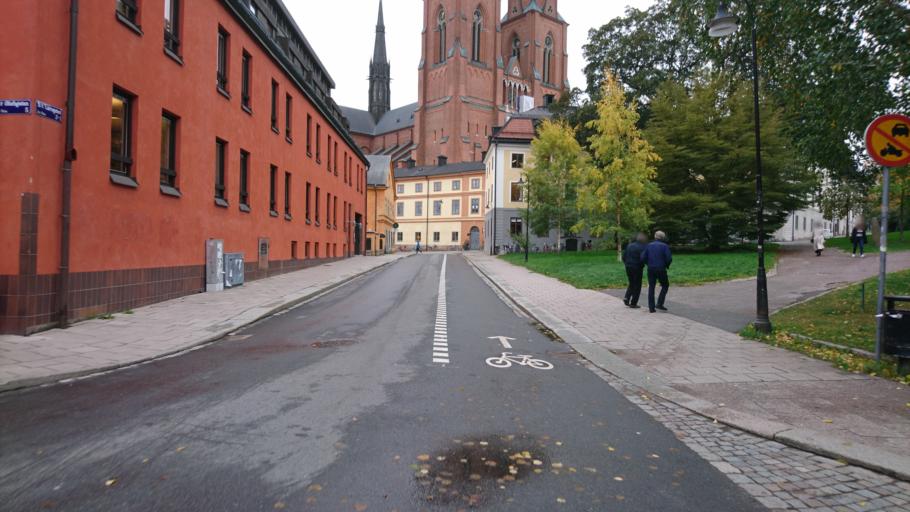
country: SE
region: Uppsala
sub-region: Uppsala Kommun
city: Uppsala
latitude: 59.8590
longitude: 17.6311
